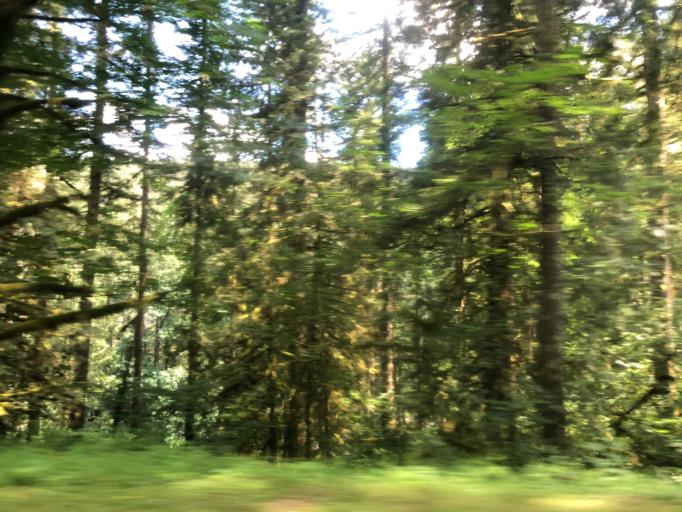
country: US
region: Oregon
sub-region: Clackamas County
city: Sandy
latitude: 45.4259
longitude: -122.2090
